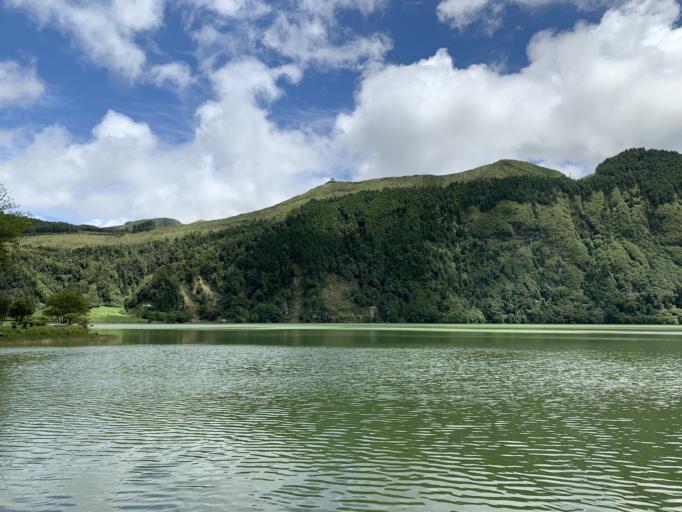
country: PT
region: Azores
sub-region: Ponta Delgada
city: Arrifes
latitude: 37.8492
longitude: -25.7931
